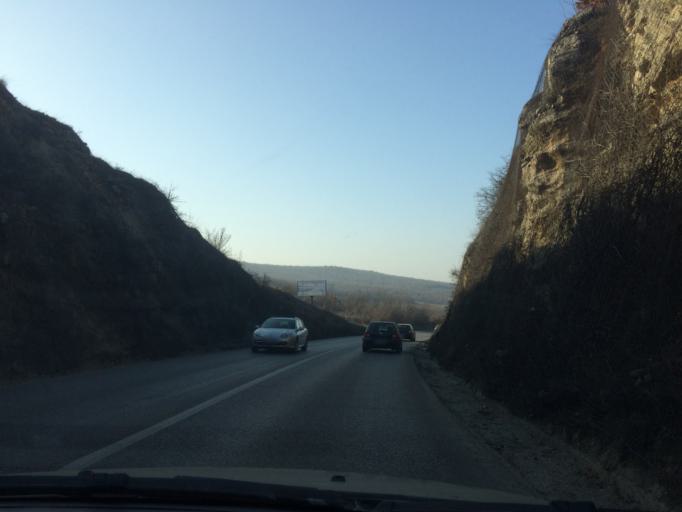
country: XK
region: Pec
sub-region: Komuna e Klines
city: Klina
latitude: 42.5944
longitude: 20.6041
